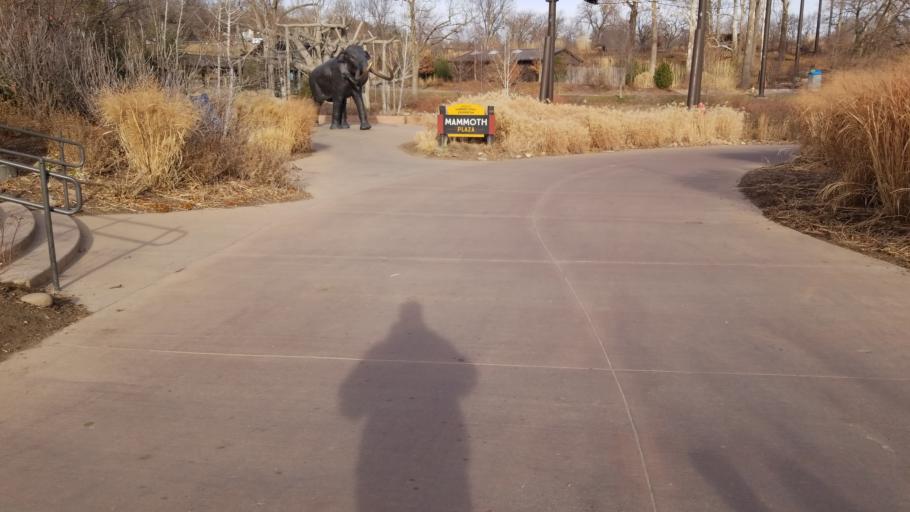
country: US
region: Nebraska
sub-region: Douglas County
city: Omaha
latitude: 41.2248
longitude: -95.9242
